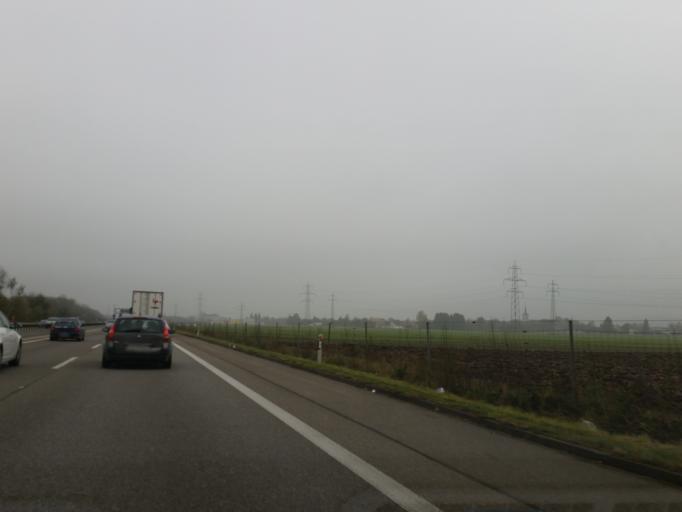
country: CH
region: Solothurn
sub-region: Bezirk Gaeu
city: Oberbuchsiten
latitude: 47.2956
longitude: 7.7557
